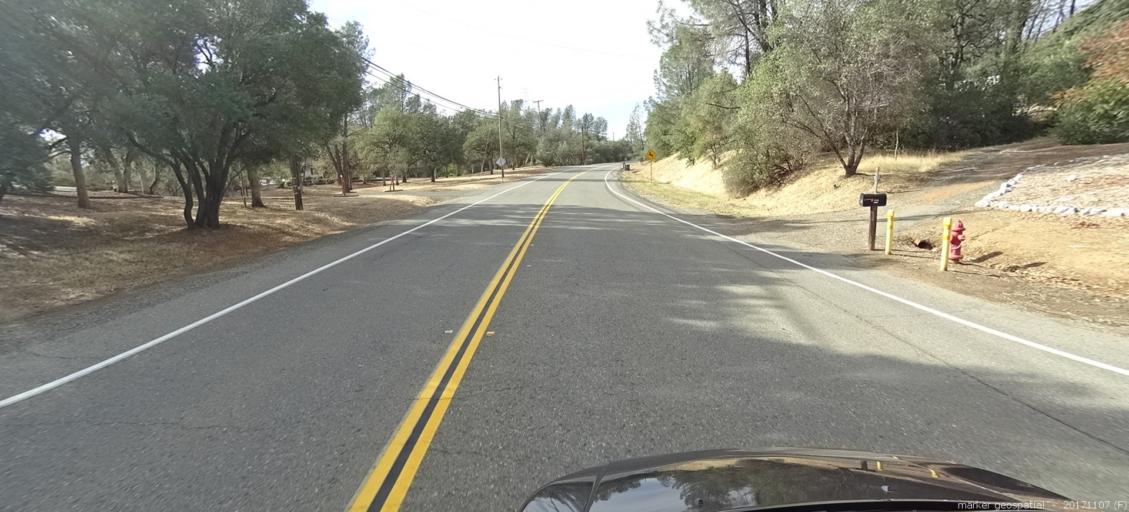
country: US
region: California
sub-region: Shasta County
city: Redding
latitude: 40.5584
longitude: -122.4351
